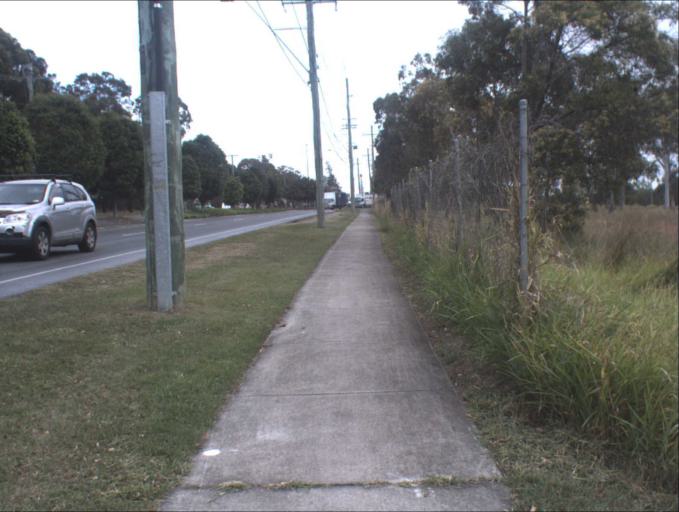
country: AU
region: Queensland
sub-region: Logan
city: Logan Reserve
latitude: -27.6770
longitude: 153.0793
